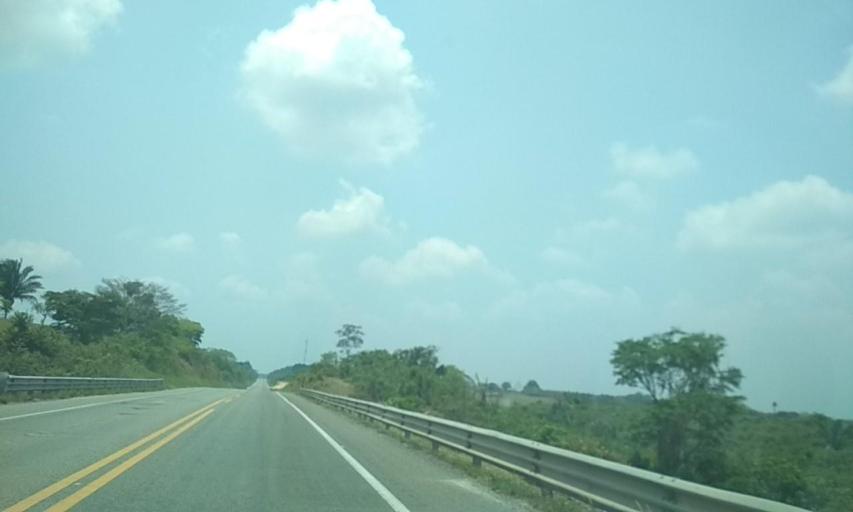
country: MX
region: Tabasco
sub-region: Huimanguillo
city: Francisco Rueda
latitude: 17.7418
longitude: -93.9831
